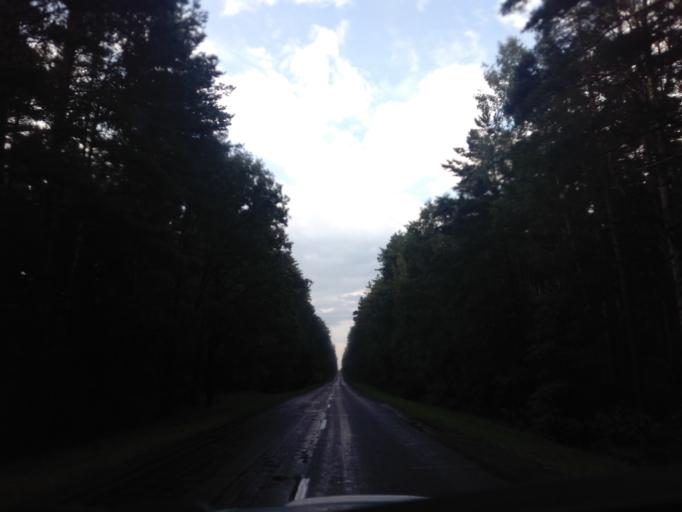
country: BY
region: Minsk
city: Uzda
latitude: 53.3598
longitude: 27.1001
